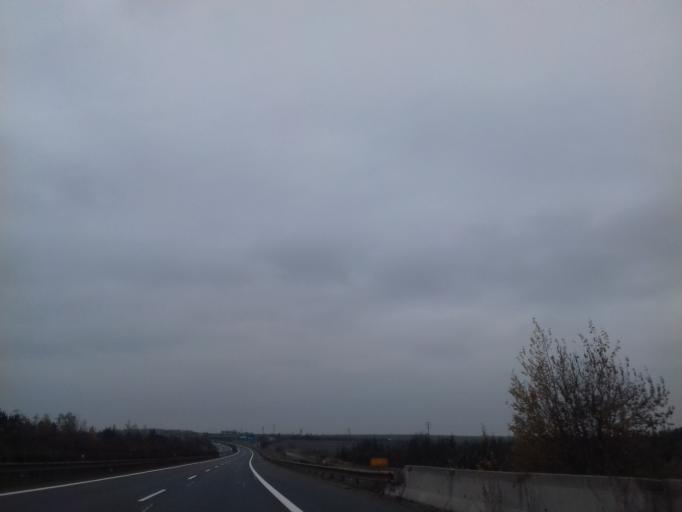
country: CZ
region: Plzensky
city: Stenovice
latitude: 49.6824
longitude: 13.3947
